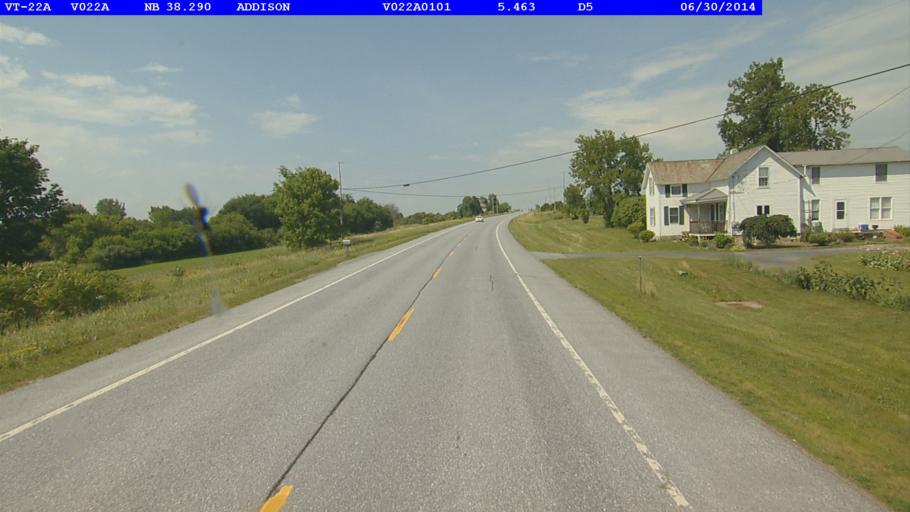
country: US
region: Vermont
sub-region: Addison County
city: Vergennes
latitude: 44.1074
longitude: -73.2953
